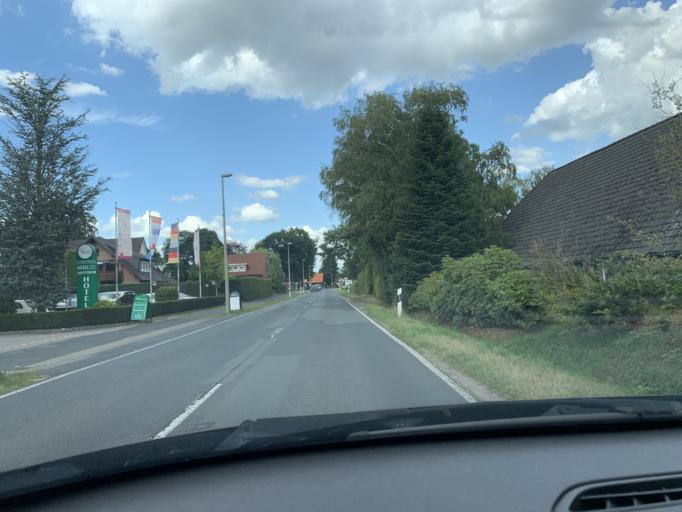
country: DE
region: Lower Saxony
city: Bad Zwischenahn
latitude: 53.1884
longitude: 8.0381
